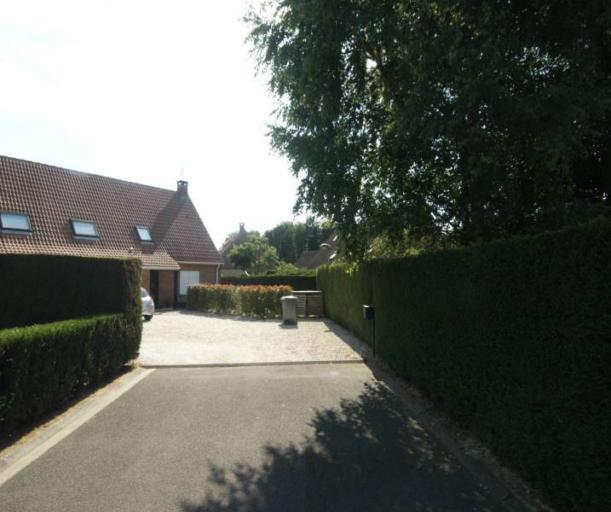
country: FR
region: Nord-Pas-de-Calais
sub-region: Departement du Nord
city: Bondues
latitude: 50.7097
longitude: 3.0717
